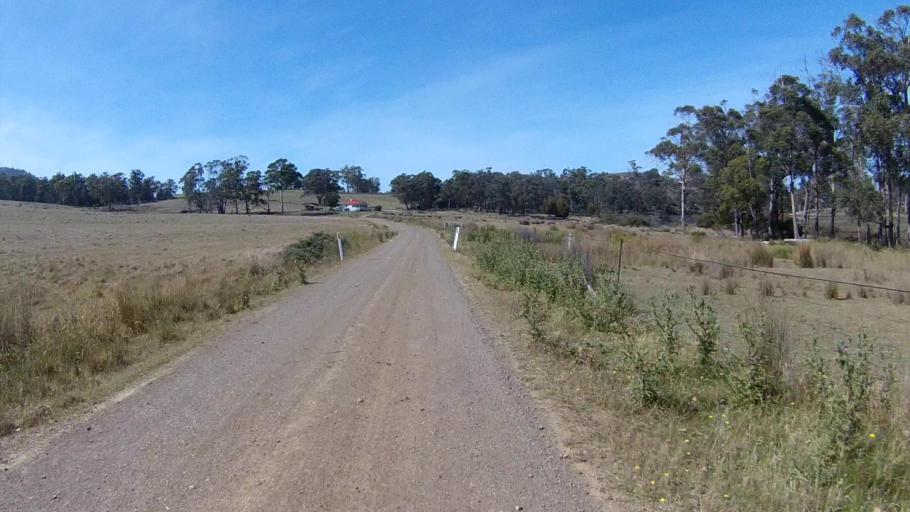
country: AU
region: Tasmania
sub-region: Sorell
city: Sorell
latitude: -42.7154
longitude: 147.5945
